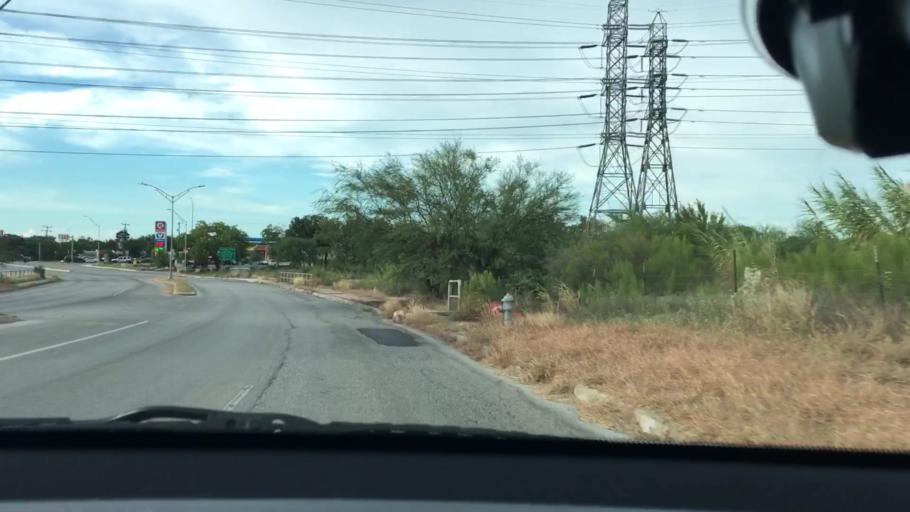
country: US
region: Texas
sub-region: Bexar County
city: Windcrest
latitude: 29.5469
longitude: -98.3748
